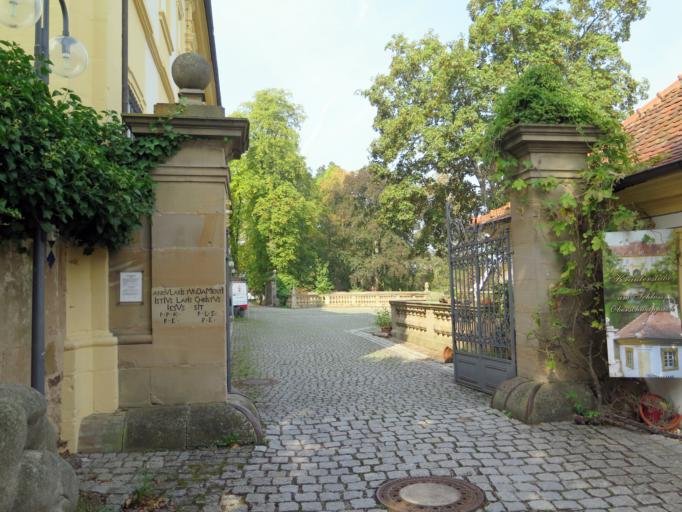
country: DE
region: Bavaria
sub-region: Regierungsbezirk Unterfranken
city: Wonfurt
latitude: 49.9685
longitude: 10.4776
